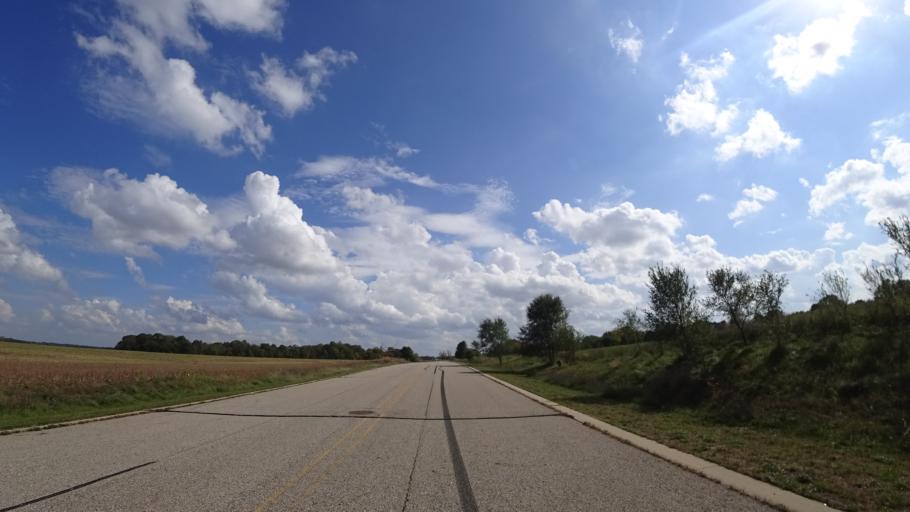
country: US
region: Michigan
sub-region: Saint Joseph County
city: Three Rivers
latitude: 41.9586
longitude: -85.6127
